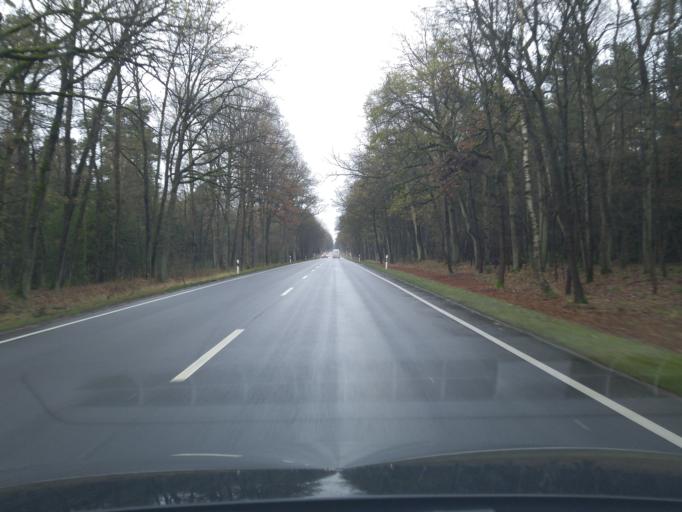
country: DE
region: Lower Saxony
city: Dedelstorf
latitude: 52.6822
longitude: 10.4716
